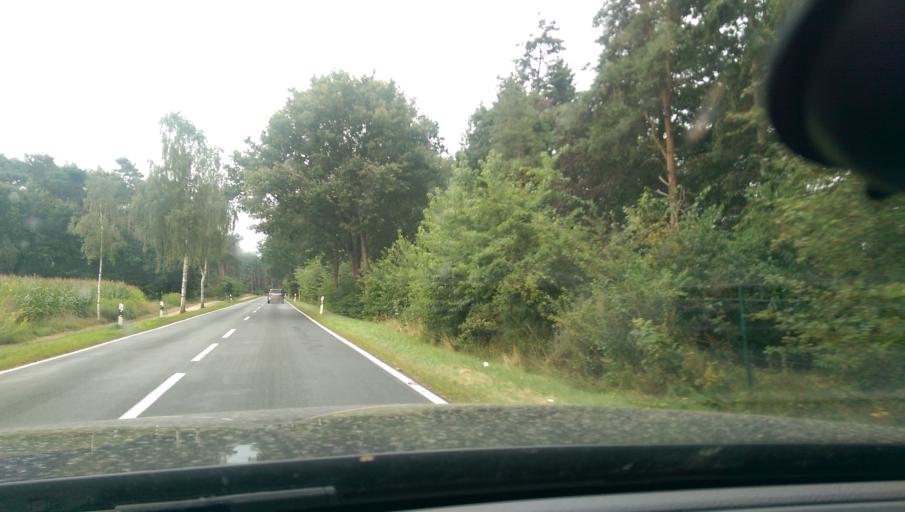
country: DE
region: Lower Saxony
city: Linsburg
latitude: 52.5211
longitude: 9.3290
